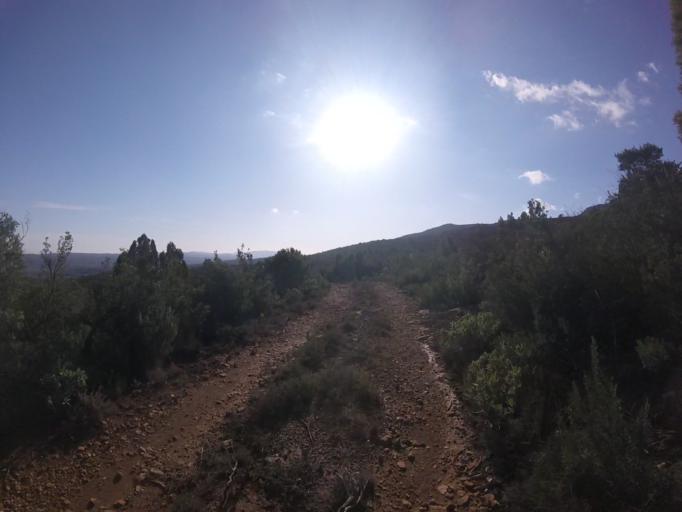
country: ES
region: Valencia
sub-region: Provincia de Castello
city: Sarratella
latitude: 40.2966
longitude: 0.0475
